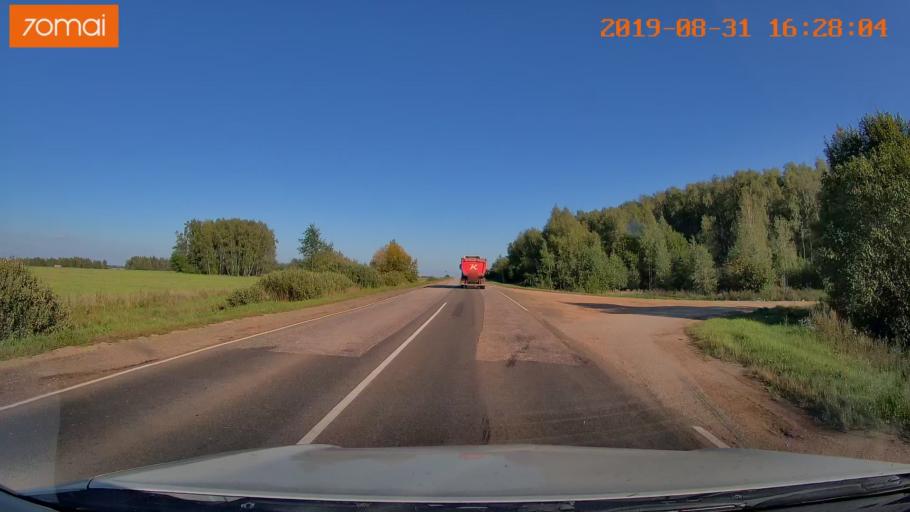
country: RU
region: Kaluga
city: Babynino
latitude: 54.5113
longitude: 35.7715
